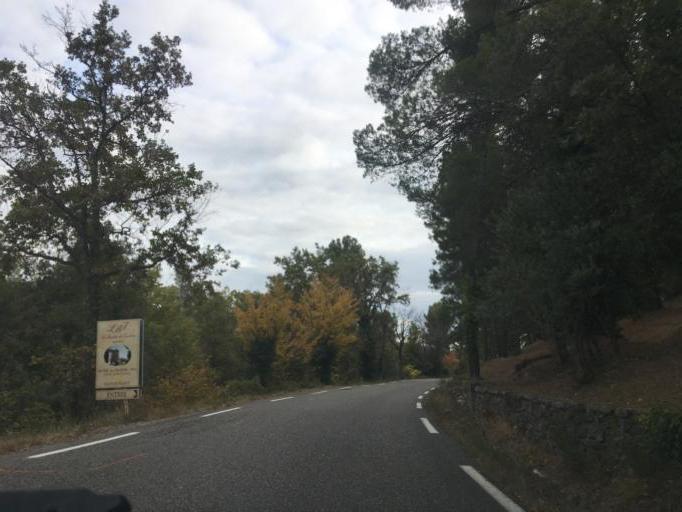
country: FR
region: Provence-Alpes-Cote d'Azur
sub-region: Departement du Var
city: Villecroze
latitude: 43.5876
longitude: 6.3078
